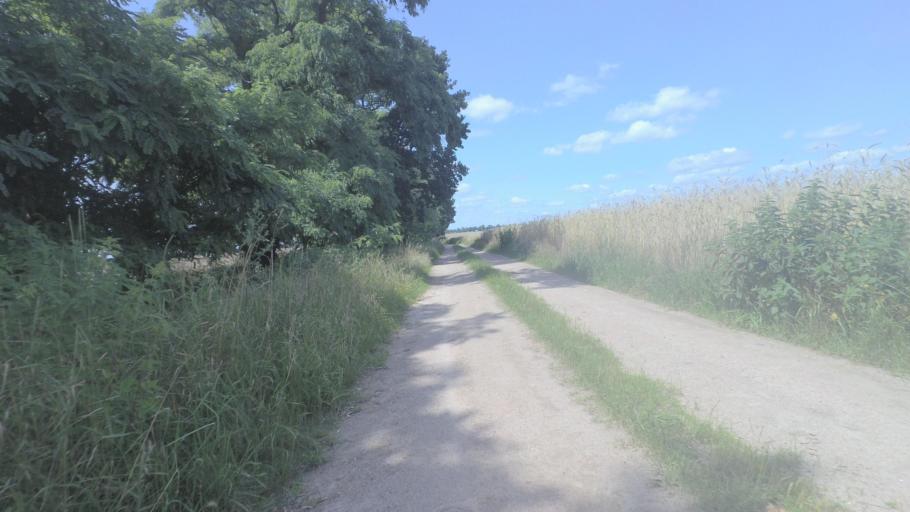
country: DE
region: Brandenburg
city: Am Mellensee
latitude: 52.2403
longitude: 13.3664
